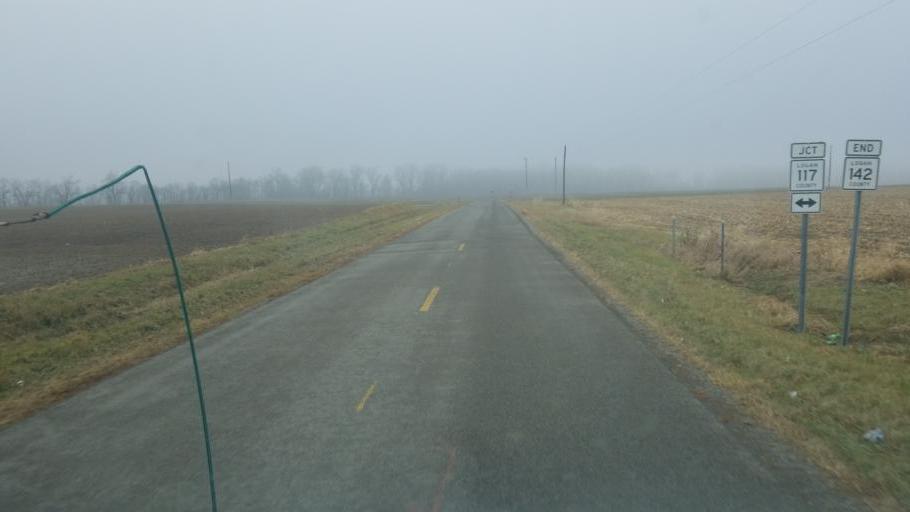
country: US
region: Ohio
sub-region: Hardin County
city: Kenton
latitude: 40.4888
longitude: -83.5459
